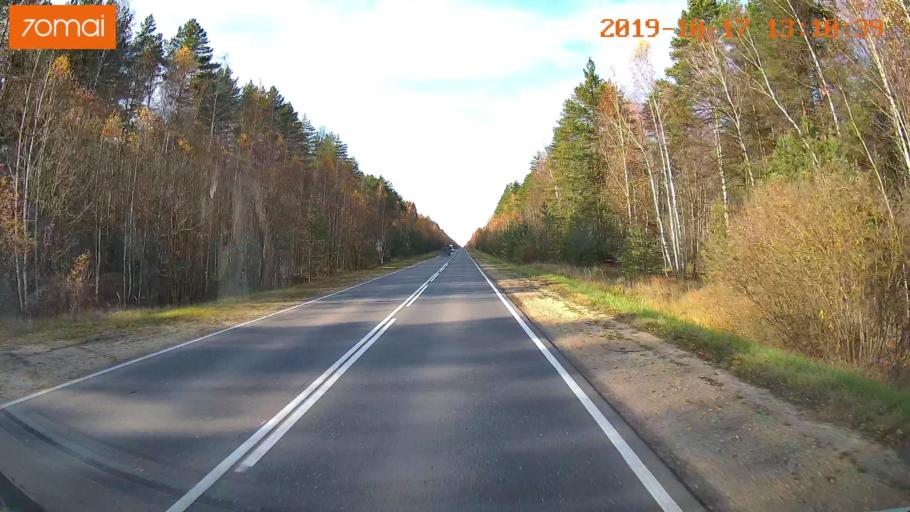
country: RU
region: Rjazan
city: Syntul
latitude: 55.0208
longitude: 41.2530
